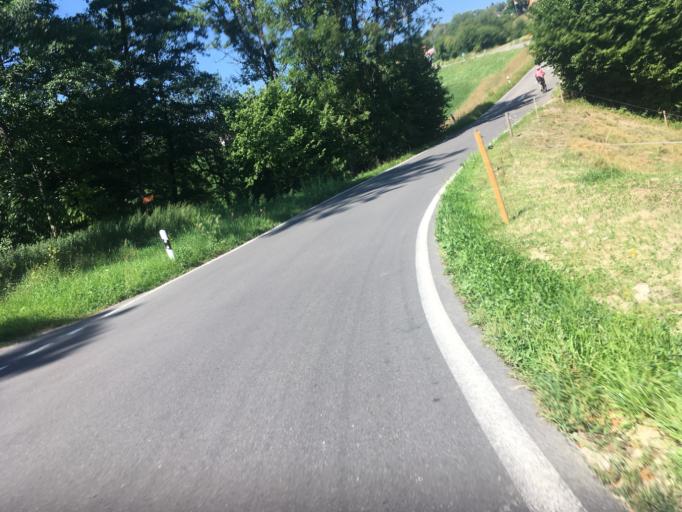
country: CH
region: Solothurn
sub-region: Bezirk Bucheggberg
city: Messen
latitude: 47.0847
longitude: 7.4734
